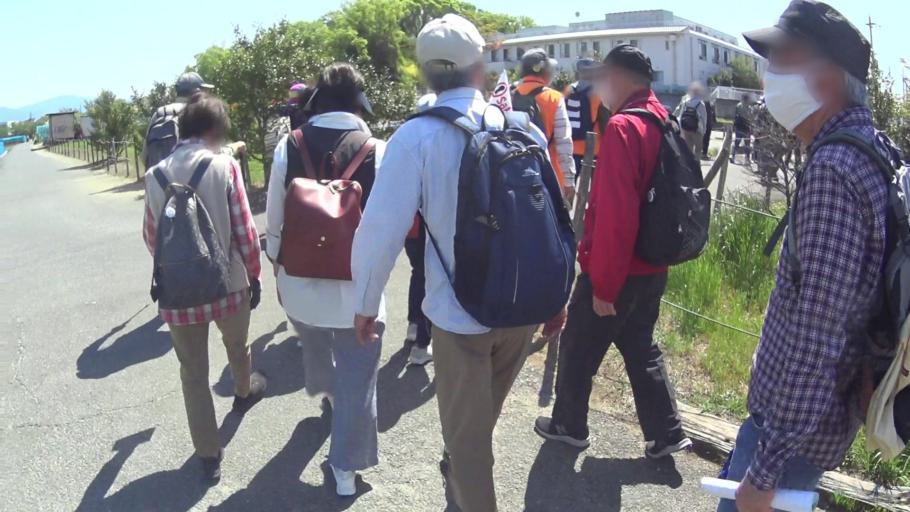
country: JP
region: Osaka
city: Kashihara
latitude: 34.5631
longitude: 135.6058
